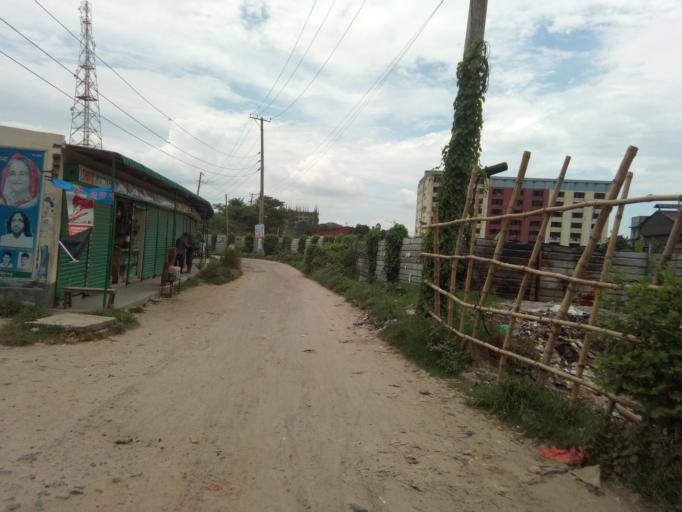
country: BD
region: Dhaka
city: Paltan
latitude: 23.7186
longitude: 90.4825
